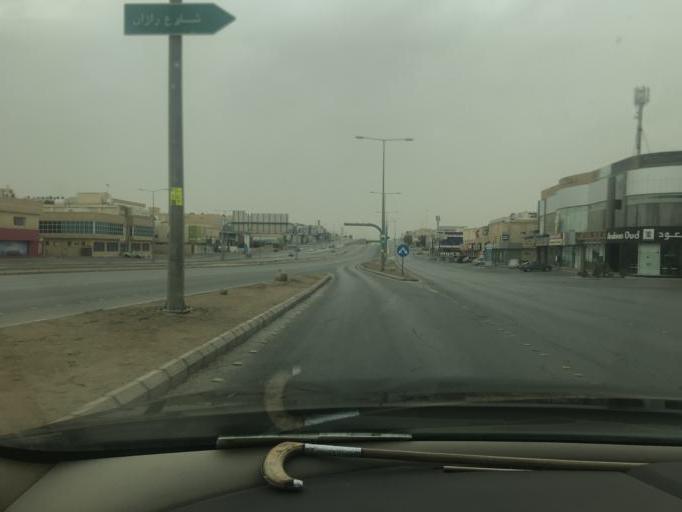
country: SA
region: Ar Riyad
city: Riyadh
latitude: 24.7726
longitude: 46.7108
